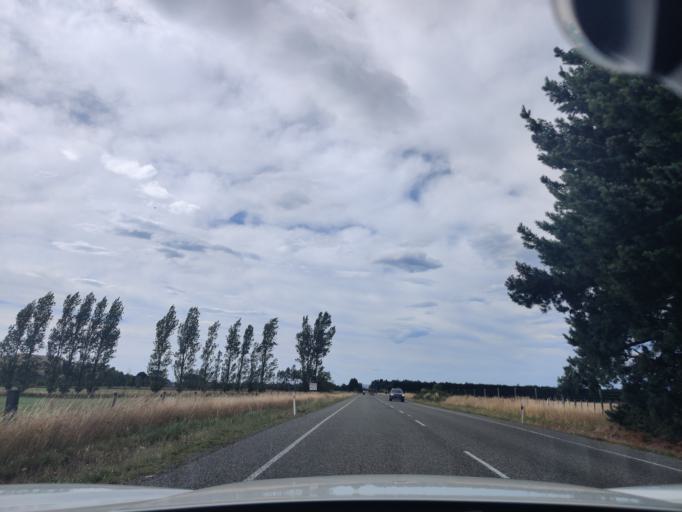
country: NZ
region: Wellington
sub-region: Masterton District
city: Masterton
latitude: -40.8539
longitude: 175.6380
